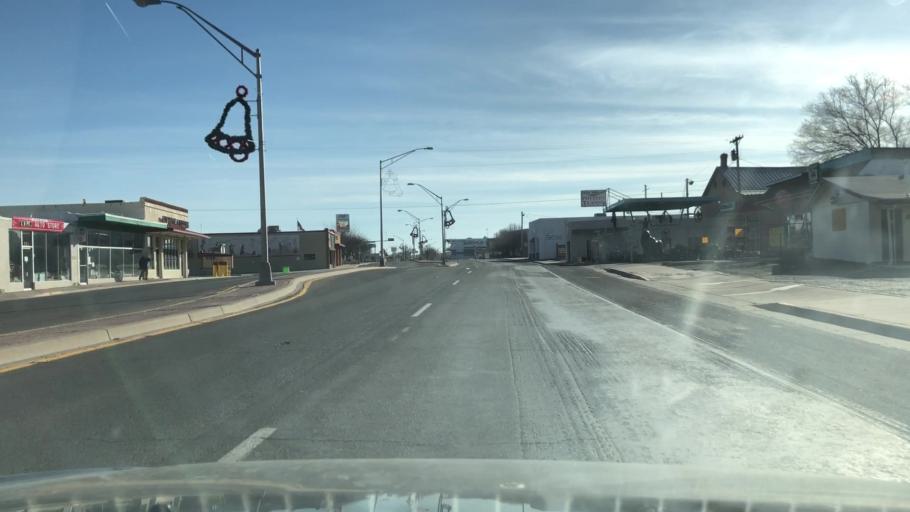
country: US
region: New Mexico
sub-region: Socorro County
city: Socorro
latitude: 34.0592
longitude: -106.8918
